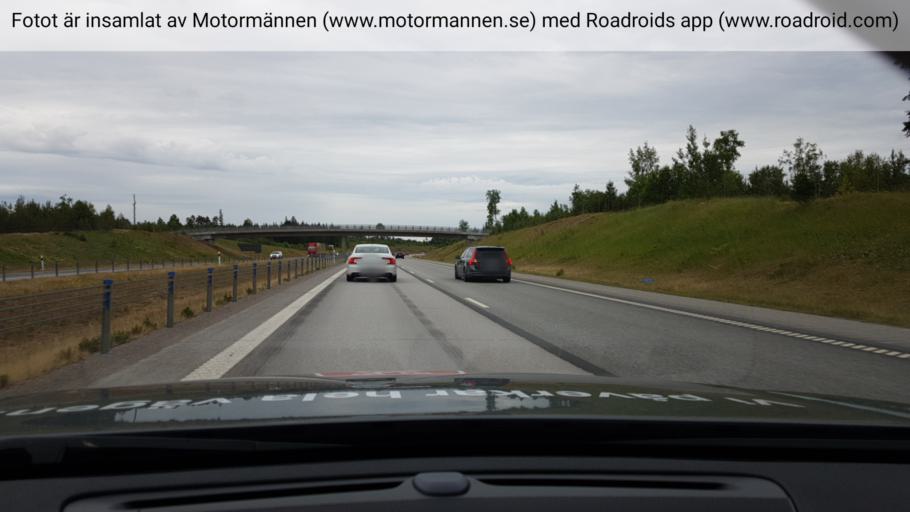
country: SE
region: Uppsala
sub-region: Uppsala Kommun
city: Gamla Uppsala
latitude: 59.9355
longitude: 17.6604
